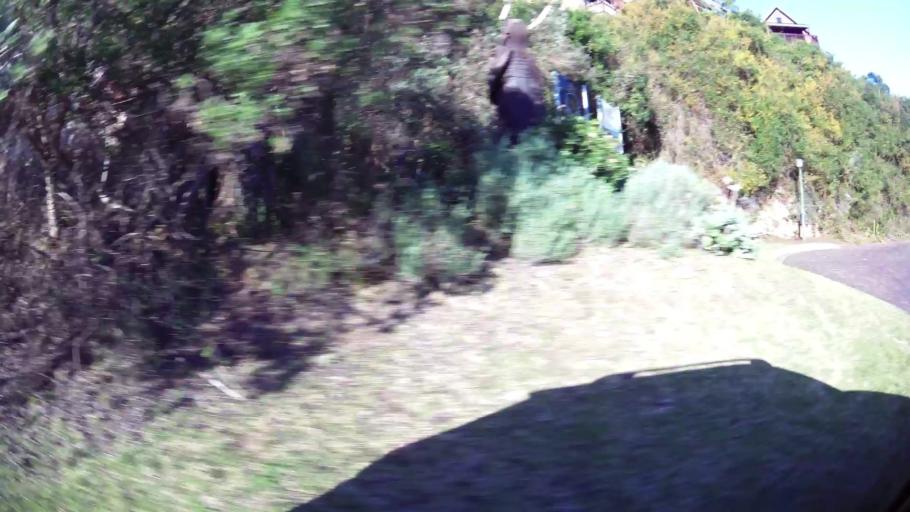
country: ZA
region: Western Cape
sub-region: Eden District Municipality
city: George
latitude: -33.9915
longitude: 22.5768
